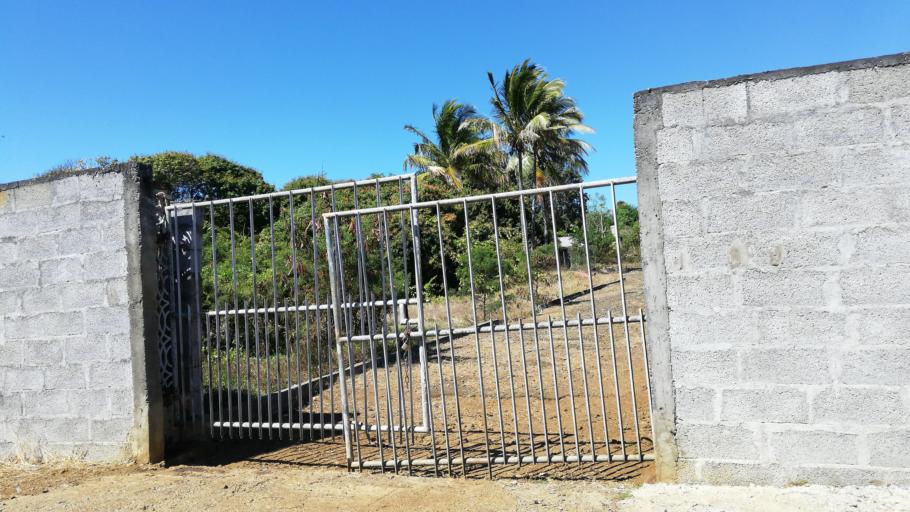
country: MU
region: Moka
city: Moka
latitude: -20.2284
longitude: 57.4732
